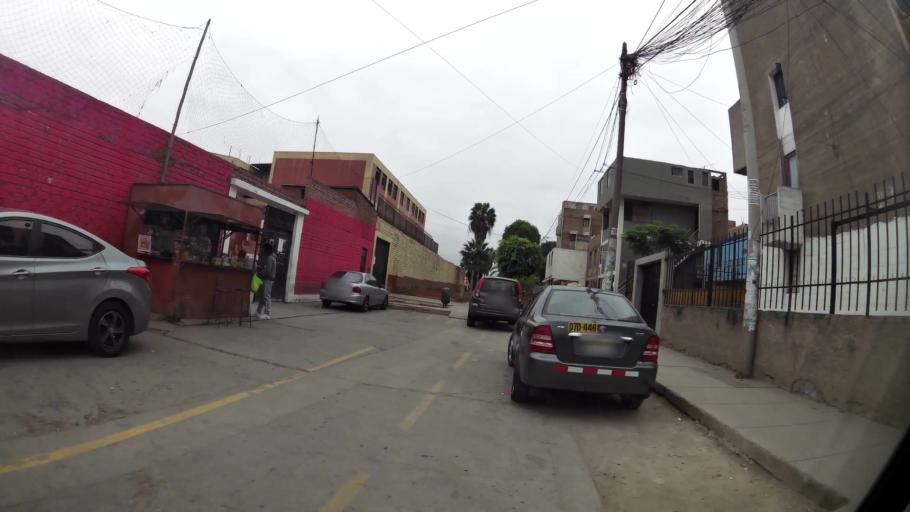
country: PE
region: Lima
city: Lima
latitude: -12.0527
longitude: -77.0693
